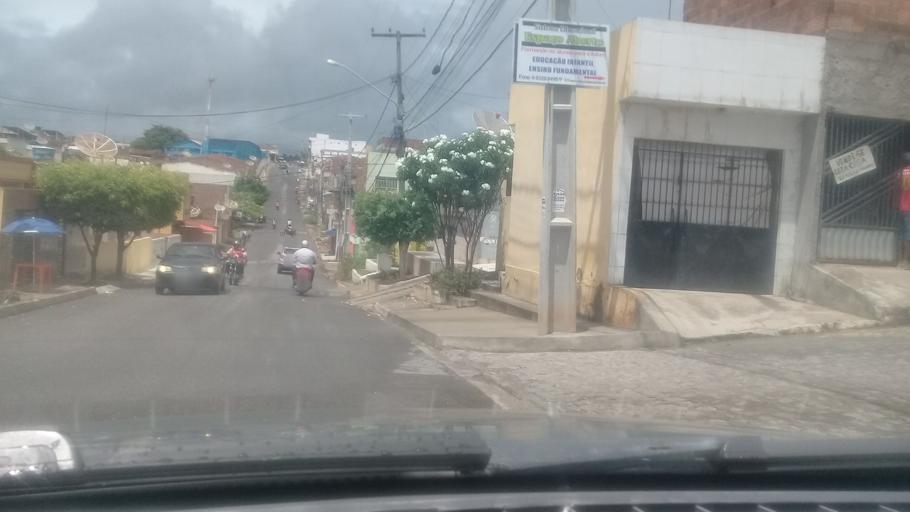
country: BR
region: Pernambuco
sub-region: Vitoria De Santo Antao
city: Vitoria de Santo Antao
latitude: -8.1251
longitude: -35.2907
